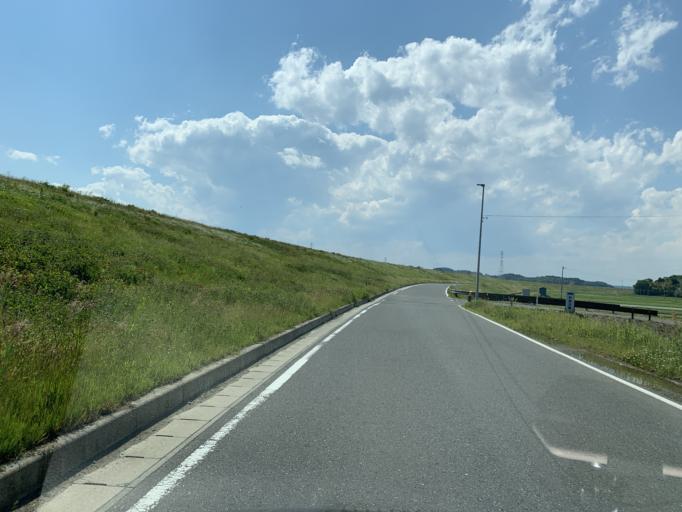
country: JP
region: Miyagi
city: Yamoto
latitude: 38.4214
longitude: 141.1328
